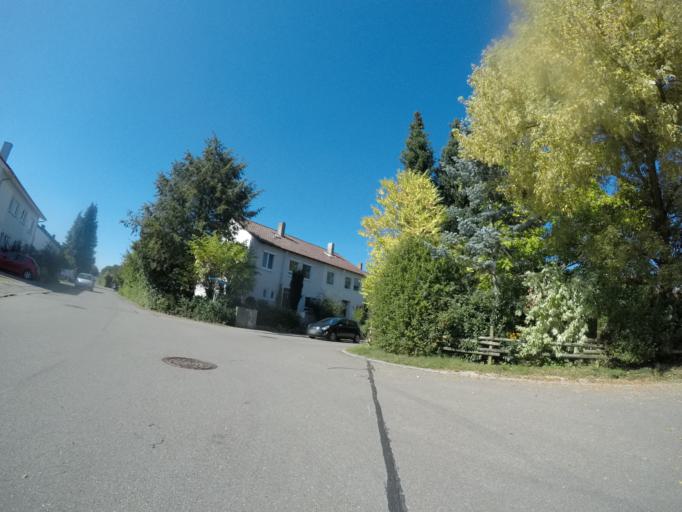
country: DE
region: Baden-Wuerttemberg
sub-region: Tuebingen Region
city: Kusterdingen
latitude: 48.4996
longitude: 9.0901
